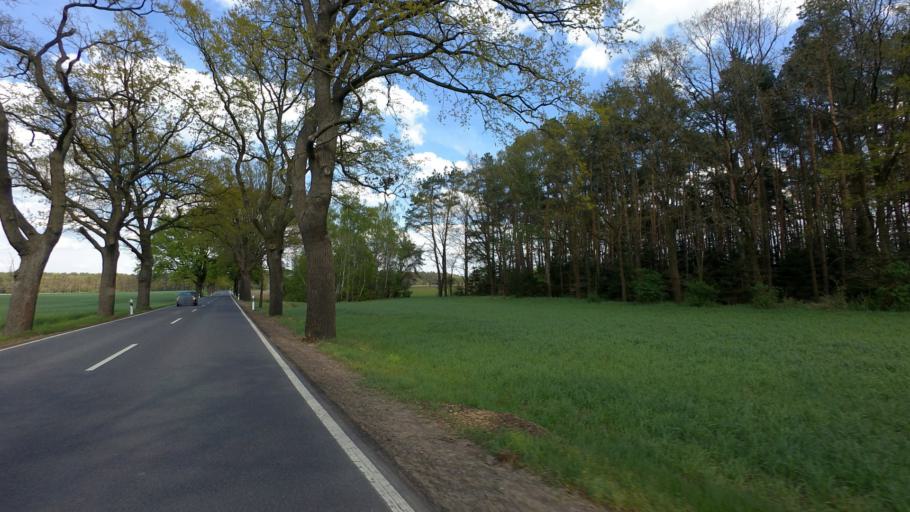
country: DE
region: Brandenburg
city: Marienwerder
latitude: 52.8748
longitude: 13.5410
